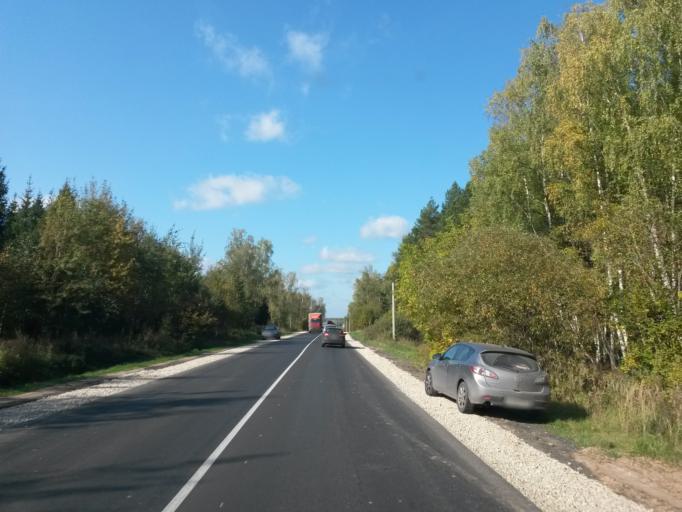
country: RU
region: Moskovskaya
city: Lyubuchany
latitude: 55.2476
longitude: 37.5754
